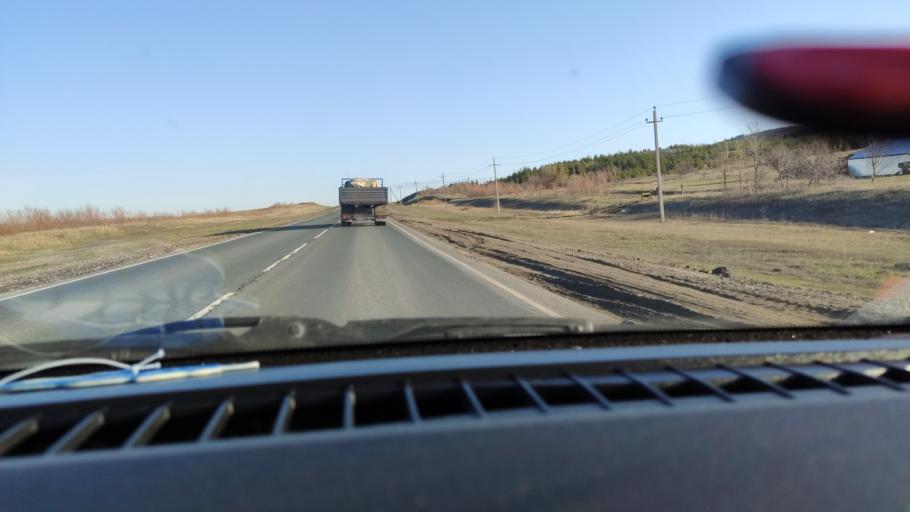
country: RU
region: Saratov
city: Alekseyevka
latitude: 52.2975
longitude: 47.9283
